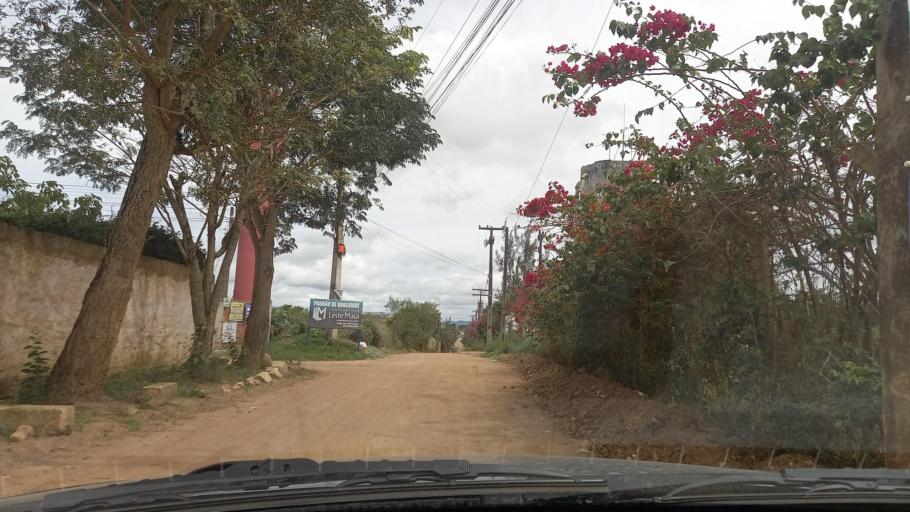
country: BR
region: Pernambuco
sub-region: Gravata
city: Gravata
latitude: -8.1916
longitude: -35.5911
